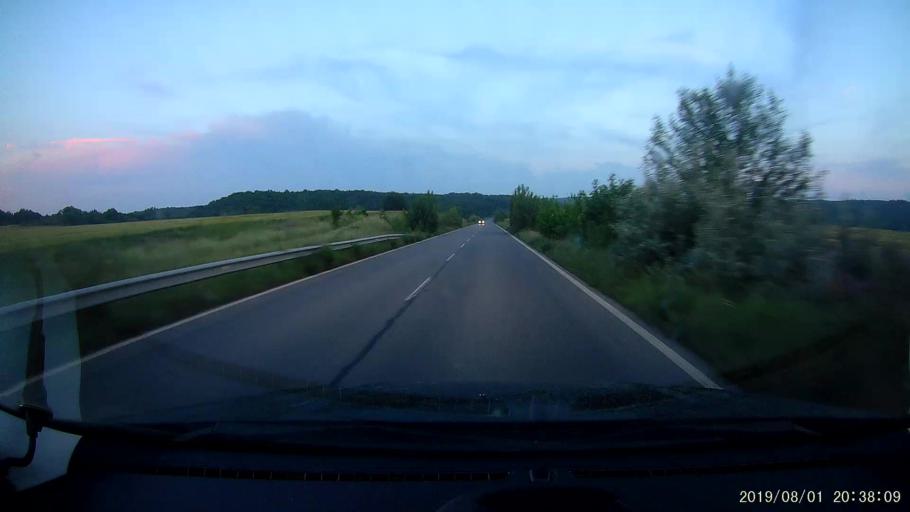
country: BG
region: Yambol
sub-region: Obshtina Elkhovo
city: Elkhovo
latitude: 42.0325
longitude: 26.5988
